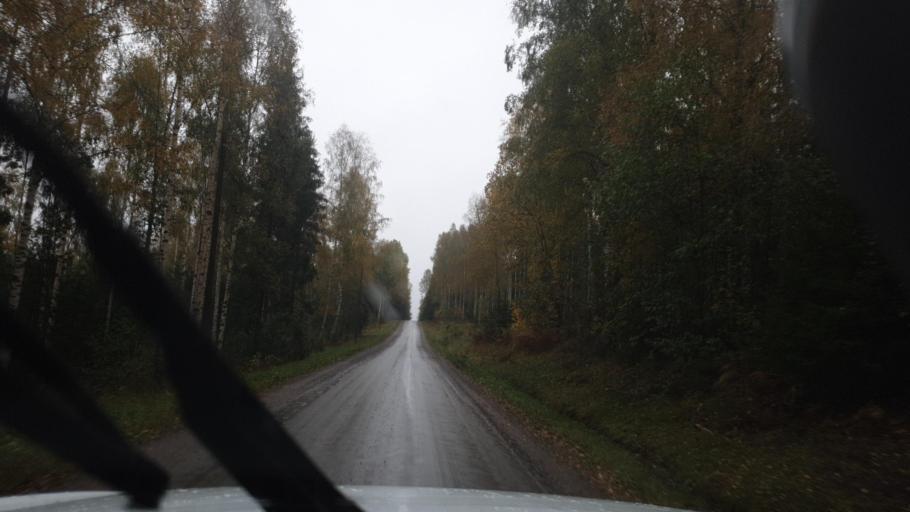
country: SE
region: Vaermland
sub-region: Eda Kommun
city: Amotfors
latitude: 59.7521
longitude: 12.2711
